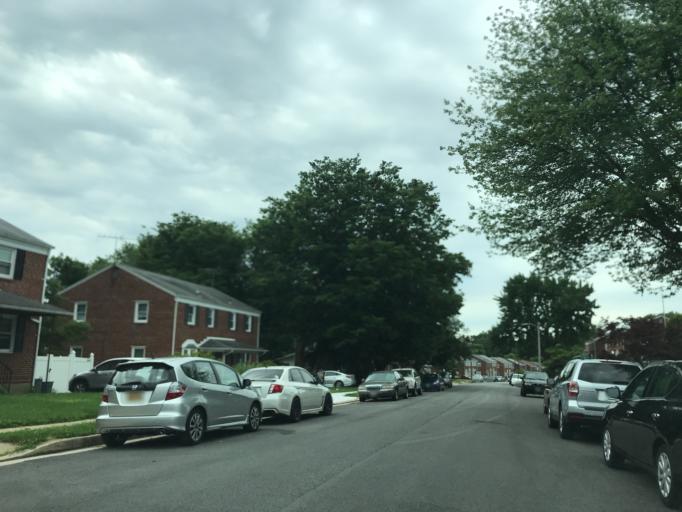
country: US
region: Maryland
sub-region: Baltimore County
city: Overlea
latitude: 39.3617
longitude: -76.5094
